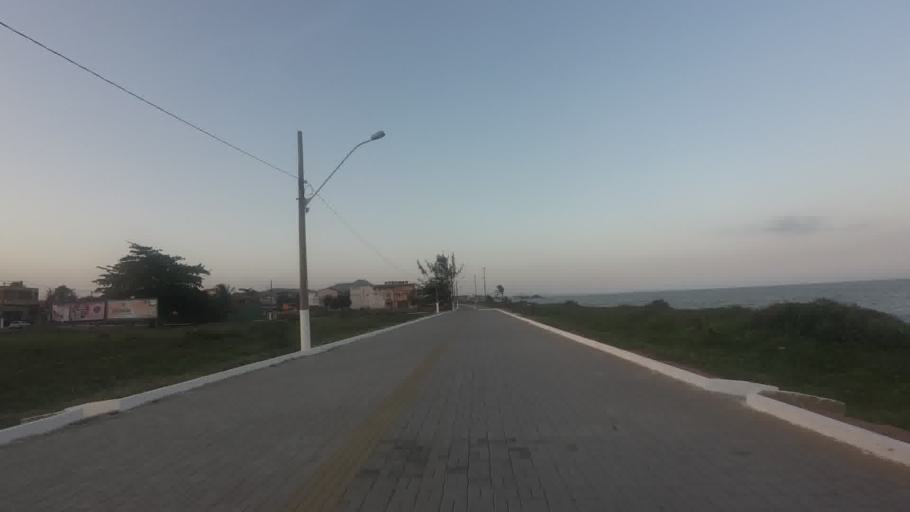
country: BR
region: Espirito Santo
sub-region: Piuma
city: Piuma
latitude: -20.9135
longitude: -40.7856
